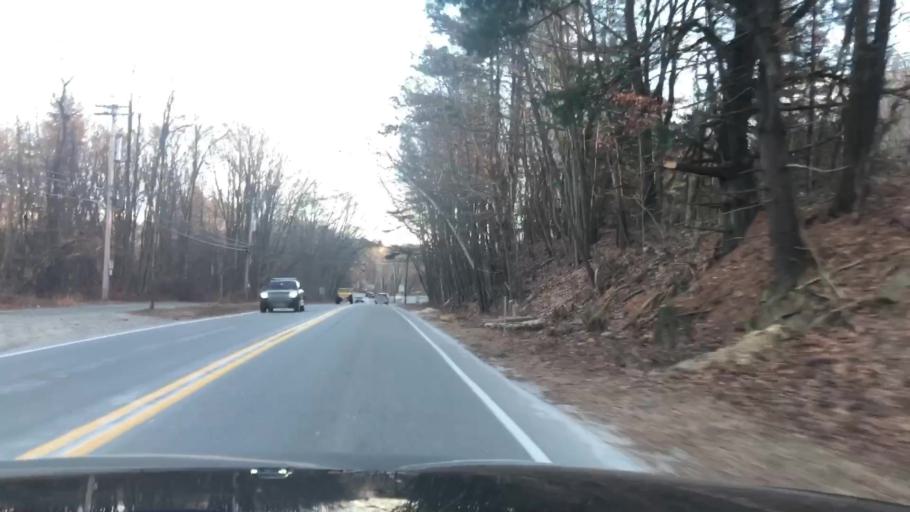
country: US
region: Massachusetts
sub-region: Worcester County
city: Bolton
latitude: 42.4391
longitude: -71.6182
